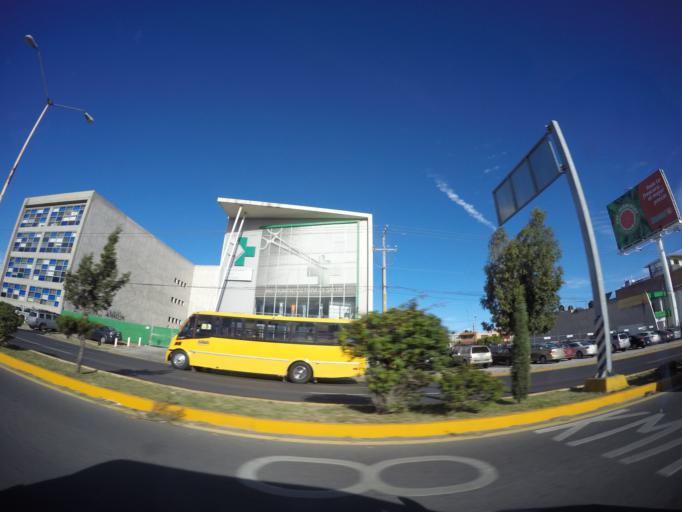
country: MX
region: San Luis Potosi
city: Escalerillas
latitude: 22.1332
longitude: -101.0318
